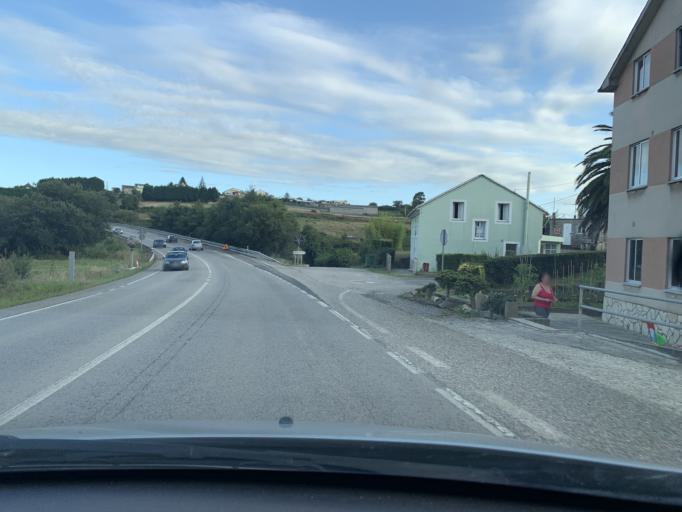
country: ES
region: Galicia
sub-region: Provincia de Lugo
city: Foz
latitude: 43.5566
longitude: -7.2706
